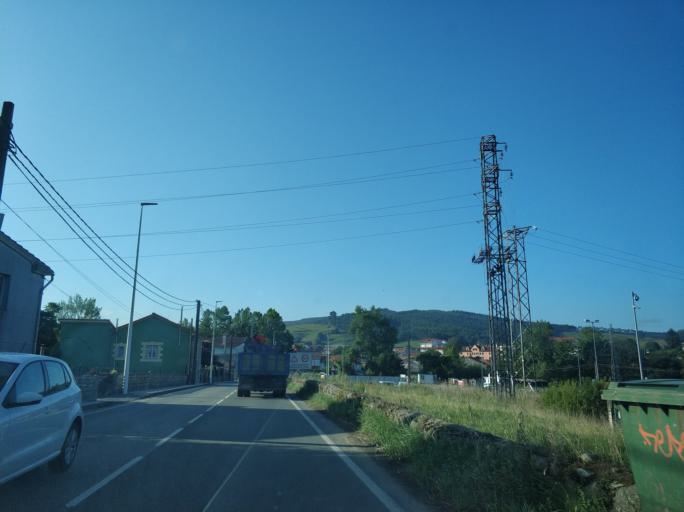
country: ES
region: Cantabria
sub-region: Provincia de Cantabria
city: Puente Viesgo
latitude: 43.3596
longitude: -3.9561
